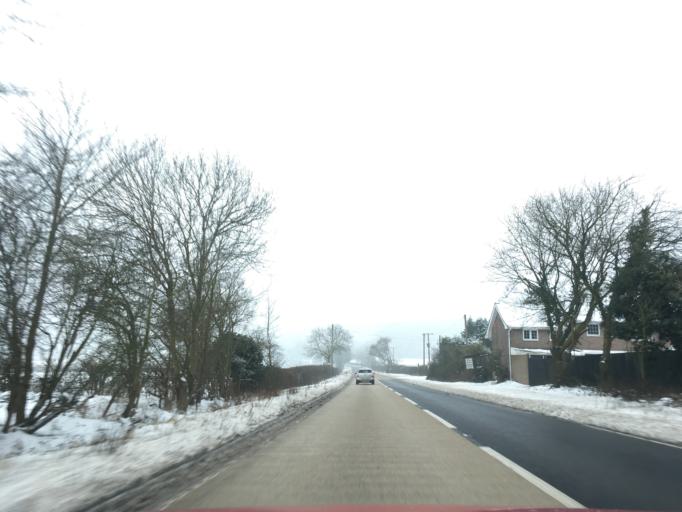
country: GB
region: England
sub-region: Warwickshire
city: Alcester
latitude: 52.2057
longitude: -1.8134
